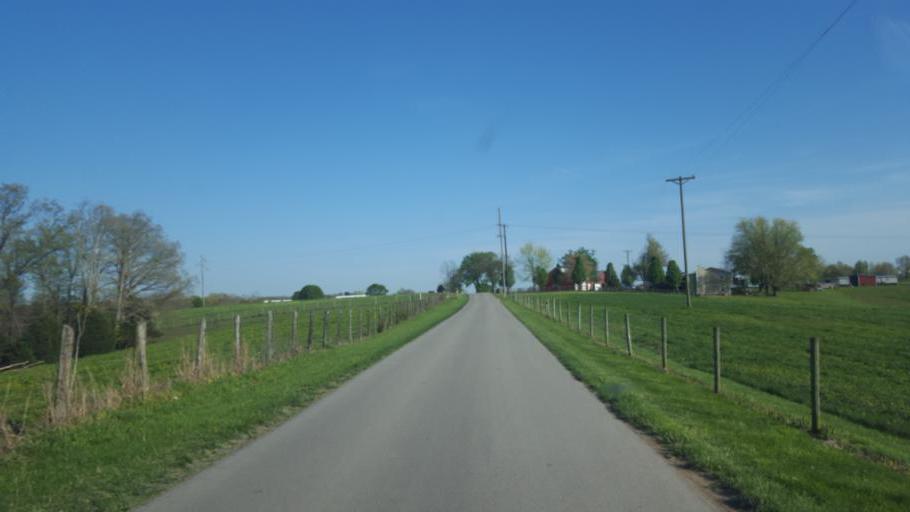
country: US
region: Kentucky
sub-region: Barren County
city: Cave City
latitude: 37.1716
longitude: -85.9896
